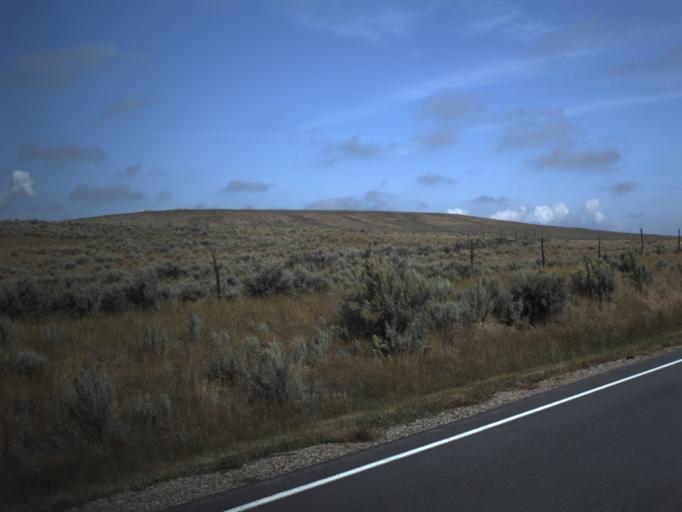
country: US
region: Utah
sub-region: Rich County
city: Randolph
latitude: 41.7584
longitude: -111.1358
